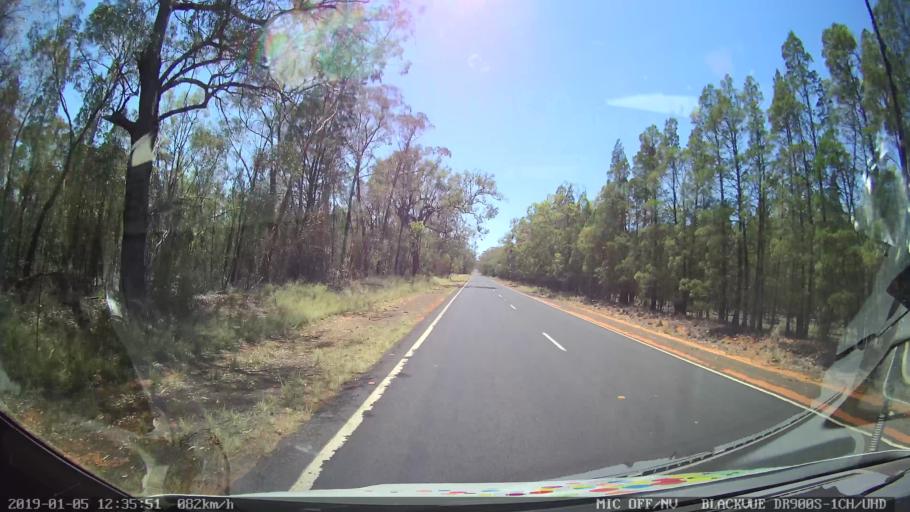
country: AU
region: New South Wales
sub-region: Warrumbungle Shire
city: Coonabarabran
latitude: -31.2086
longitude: 149.4318
